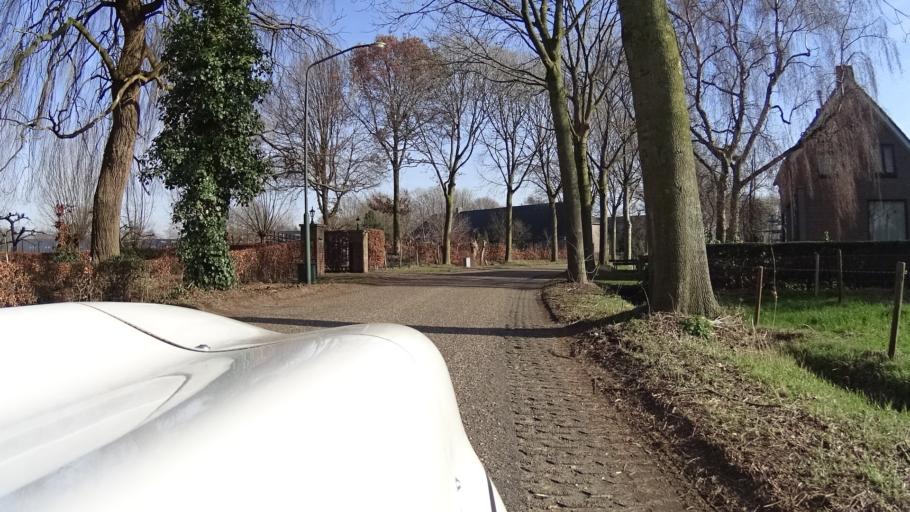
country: NL
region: North Brabant
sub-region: Gemeente Veghel
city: Erp
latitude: 51.6077
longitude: 5.6062
